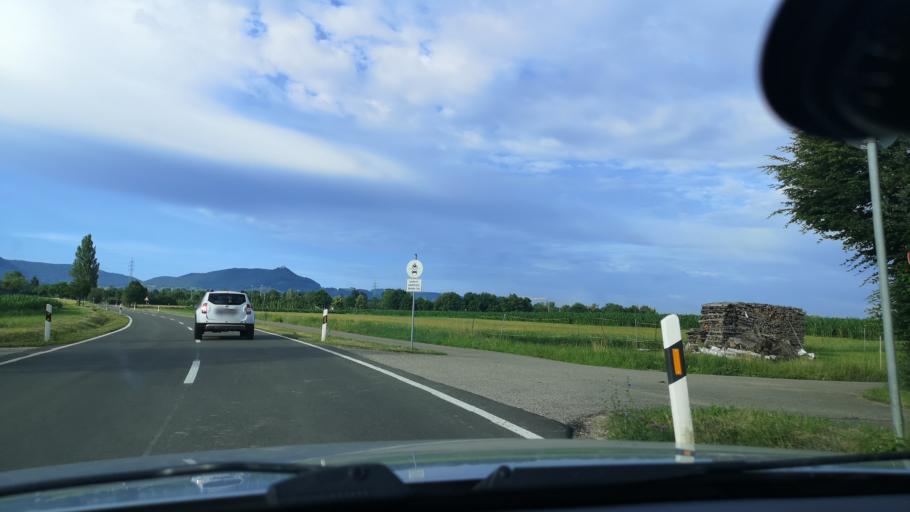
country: DE
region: Baden-Wuerttemberg
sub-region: Regierungsbezirk Stuttgart
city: Ohmden
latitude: 48.6437
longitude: 9.4963
